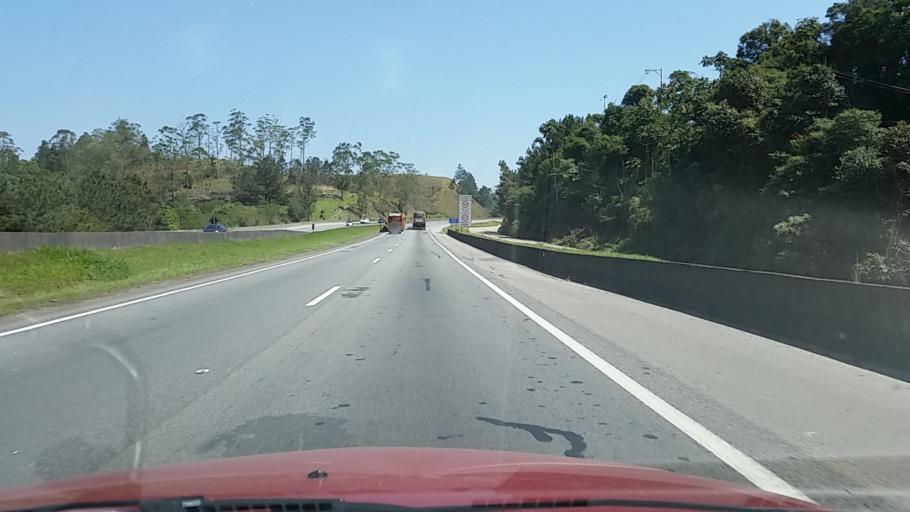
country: BR
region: Sao Paulo
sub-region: Juquitiba
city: Juquitiba
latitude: -23.9355
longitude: -47.0762
